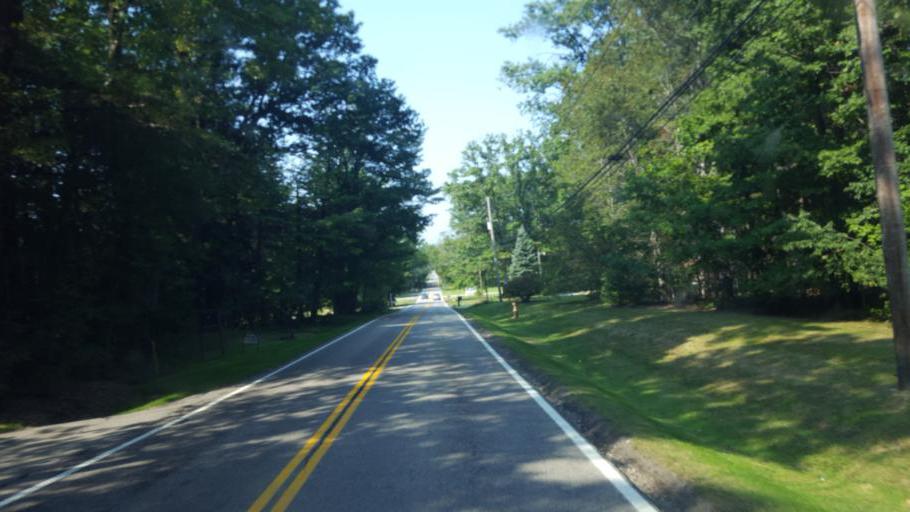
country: US
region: Ohio
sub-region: Geauga County
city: Chardon
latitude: 41.6571
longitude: -81.2108
